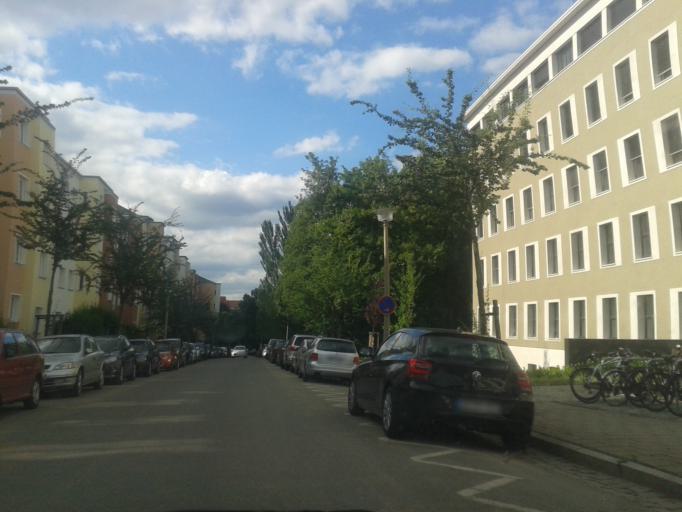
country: DE
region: Saxony
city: Dresden
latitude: 51.0277
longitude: 13.7219
